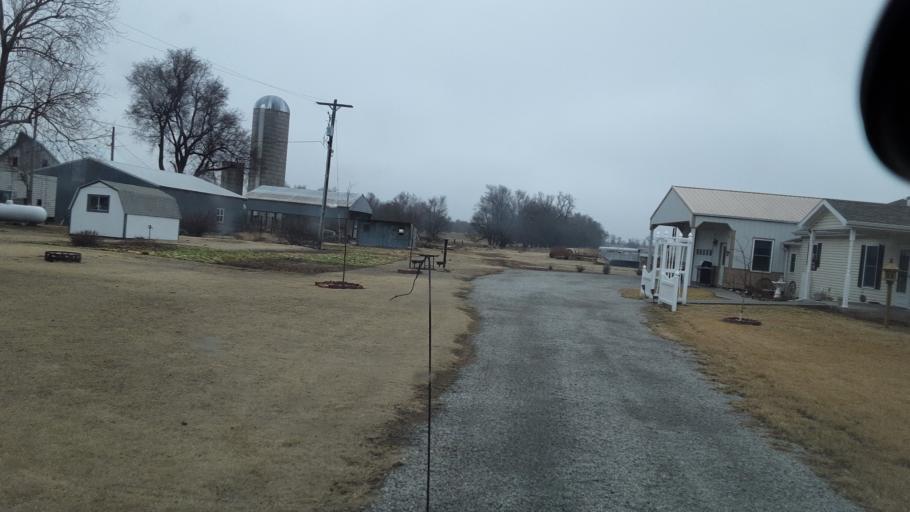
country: US
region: Kansas
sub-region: Reno County
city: South Hutchinson
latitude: 37.9557
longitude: -98.0181
